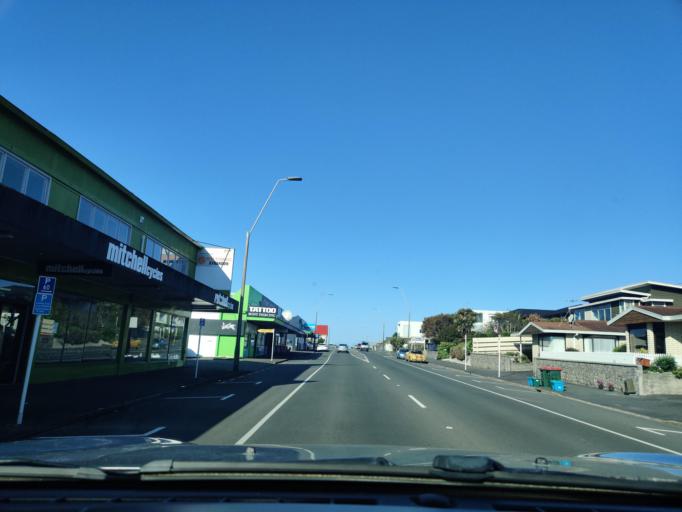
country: NZ
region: Taranaki
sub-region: New Plymouth District
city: New Plymouth
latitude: -39.0511
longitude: 174.0962
